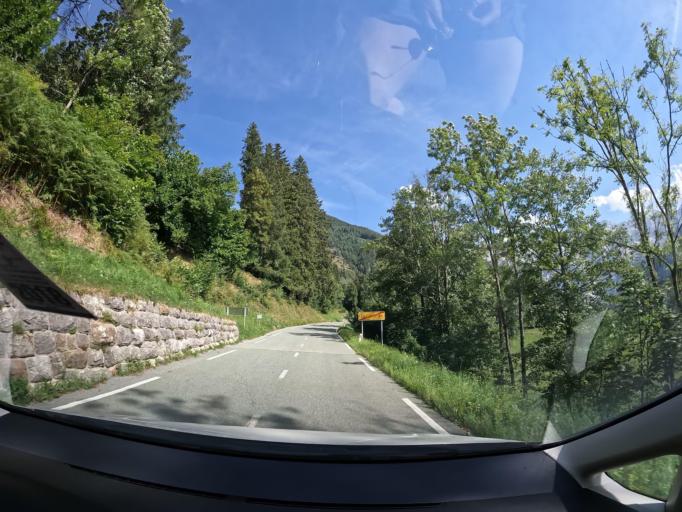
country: AT
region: Carinthia
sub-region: Politischer Bezirk Feldkirchen
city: Glanegg
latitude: 46.7117
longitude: 14.1583
